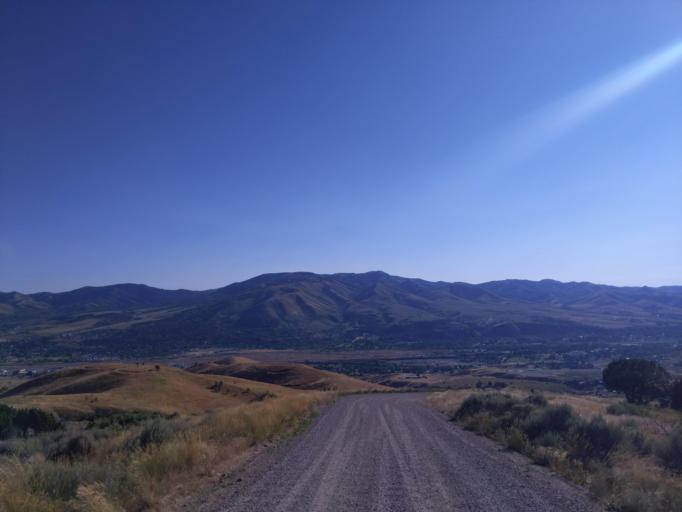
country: US
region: Idaho
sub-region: Bannock County
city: Pocatello
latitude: 42.8536
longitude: -112.3840
